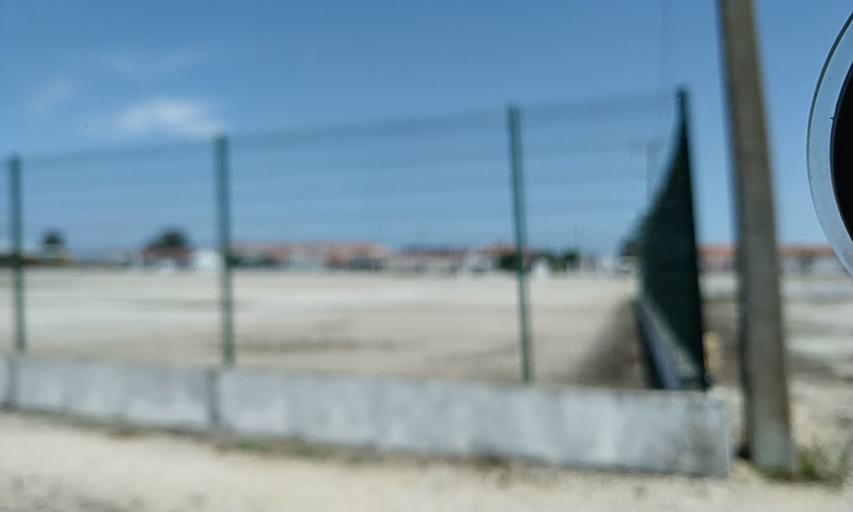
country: PT
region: Setubal
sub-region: Palmela
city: Palmela
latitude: 38.6323
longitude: -8.7468
